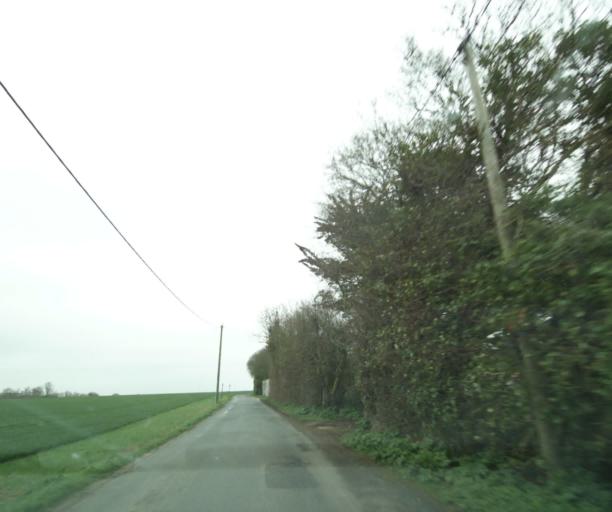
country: FR
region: Poitou-Charentes
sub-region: Departement de la Charente-Maritime
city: Puilboreau
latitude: 46.1863
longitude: -1.1353
